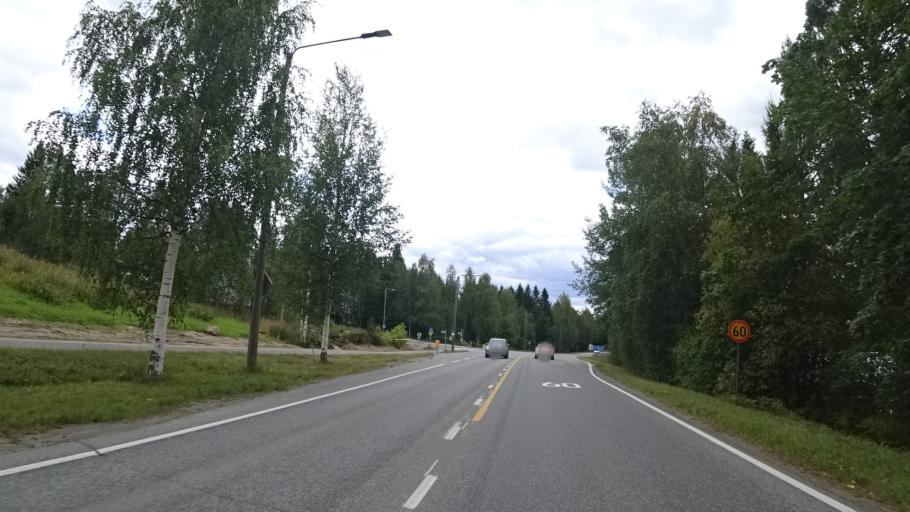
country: FI
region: North Karelia
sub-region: Joensuu
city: Ilomantsi
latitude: 62.6553
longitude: 30.9348
